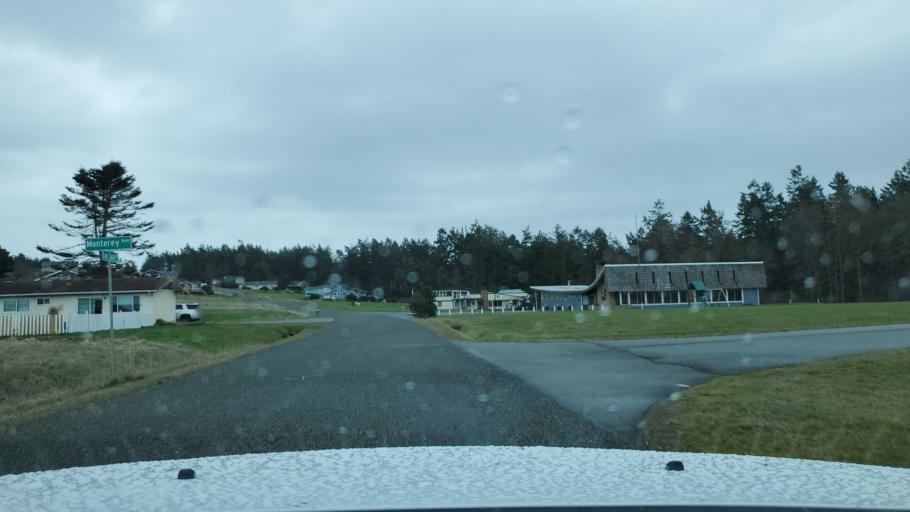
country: US
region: Washington
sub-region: Island County
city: Coupeville
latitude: 48.2337
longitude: -122.7631
